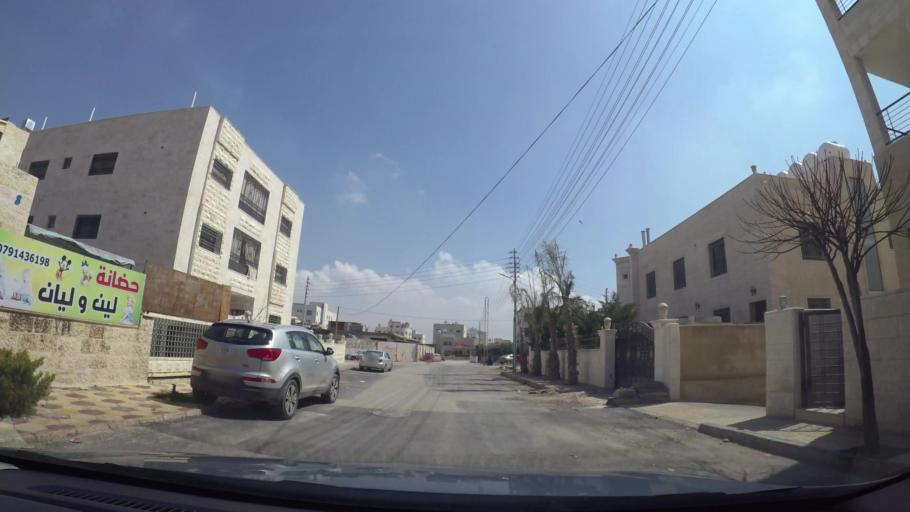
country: JO
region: Amman
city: Al Bunayyat ash Shamaliyah
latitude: 31.9021
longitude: 35.8885
